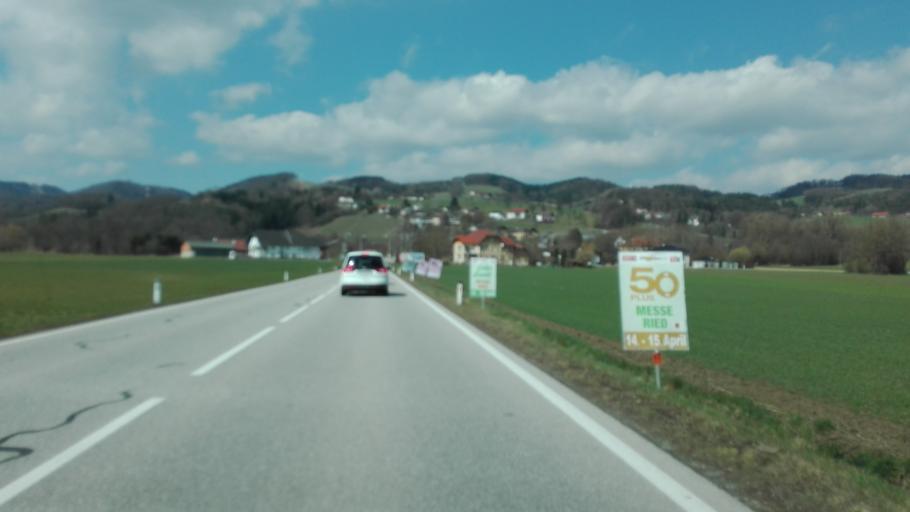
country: AT
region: Upper Austria
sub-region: Politischer Bezirk Urfahr-Umgebung
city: Feldkirchen an der Donau
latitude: 48.3706
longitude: 13.9777
